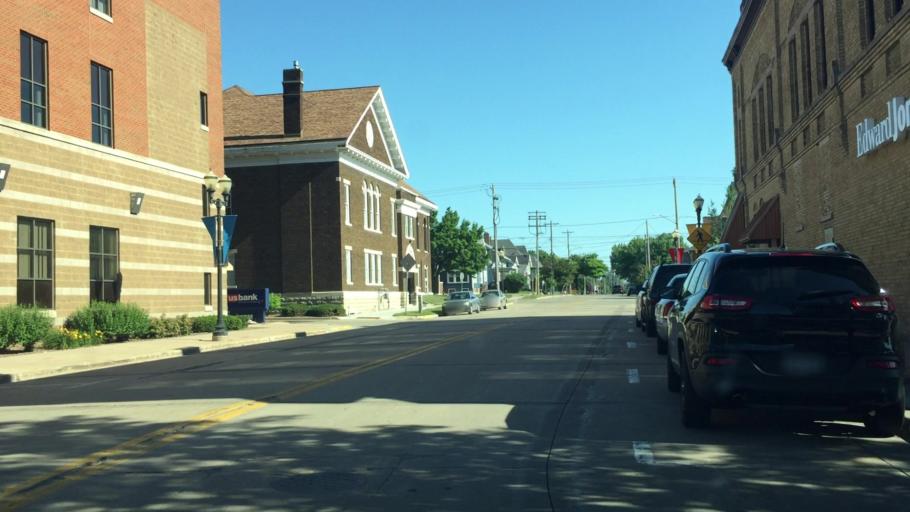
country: US
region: Wisconsin
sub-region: Winnebago County
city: Menasha
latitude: 44.2012
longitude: -88.4491
